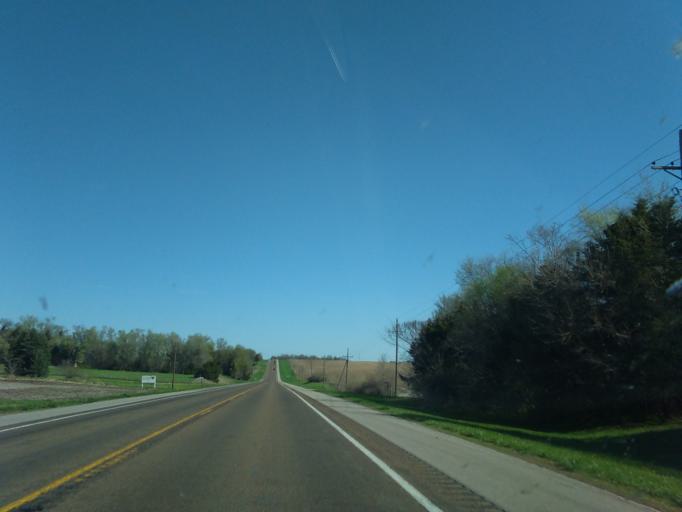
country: US
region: Nebraska
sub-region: Dodge County
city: Fremont
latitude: 41.3562
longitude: -96.5020
